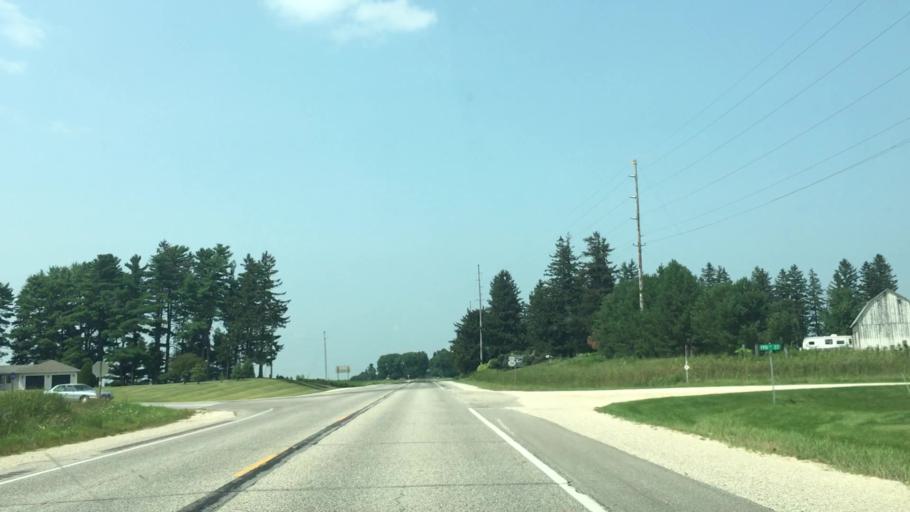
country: US
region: Iowa
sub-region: Fayette County
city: West Union
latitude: 42.9059
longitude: -91.8117
